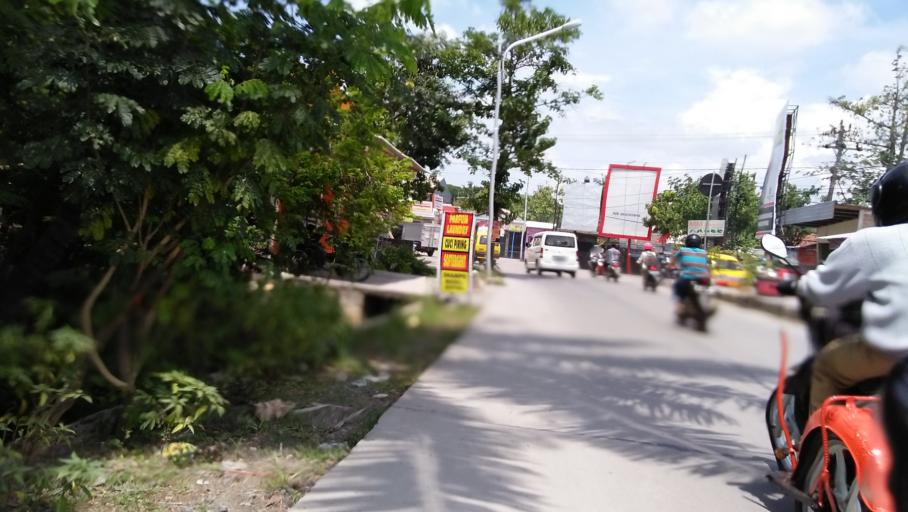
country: ID
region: Central Java
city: Semarang
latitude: -6.9697
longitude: 110.4817
